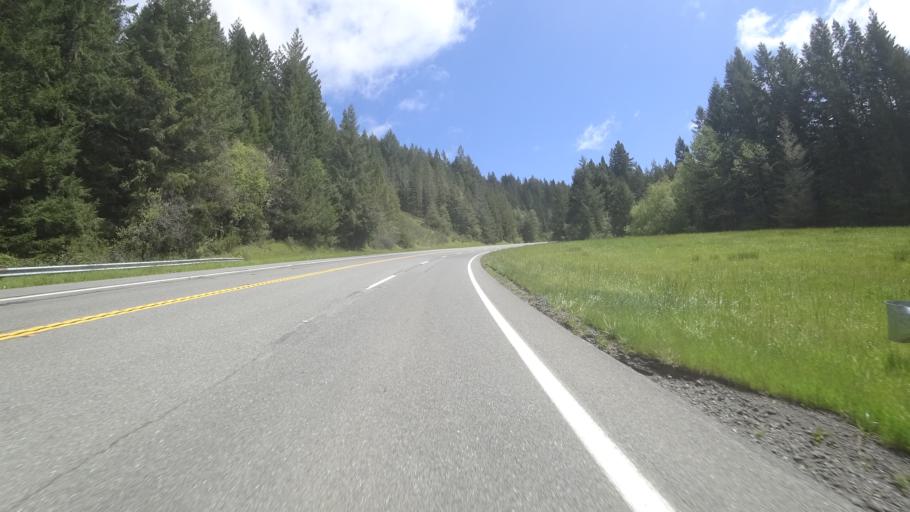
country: US
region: California
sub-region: Humboldt County
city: Blue Lake
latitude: 40.9486
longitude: -123.8970
